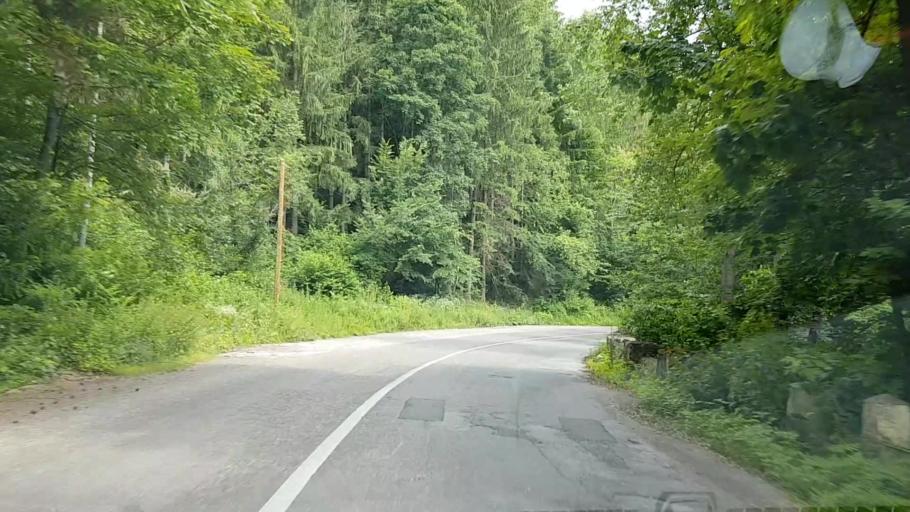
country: RO
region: Neamt
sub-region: Comuna Ceahlau
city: Ceahlau
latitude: 47.0545
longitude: 25.9731
